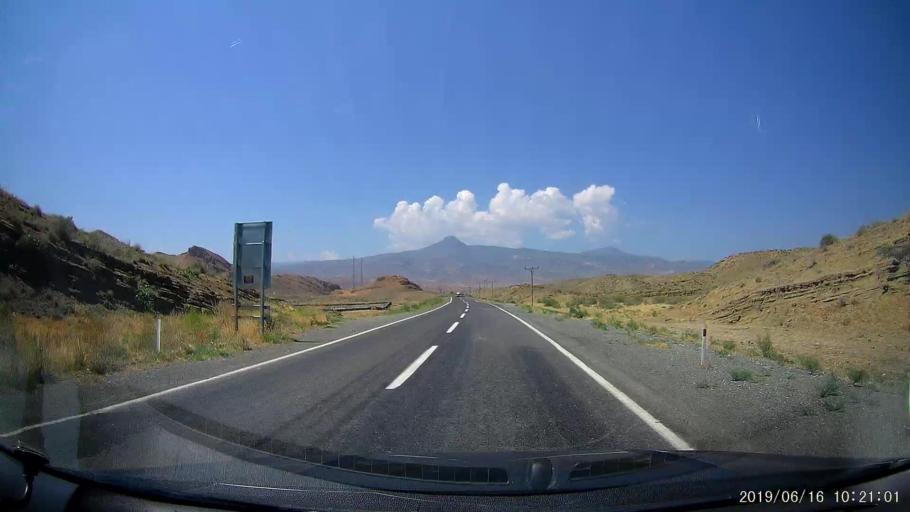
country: TR
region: Igdir
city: Tuzluca
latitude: 40.1421
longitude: 43.6415
